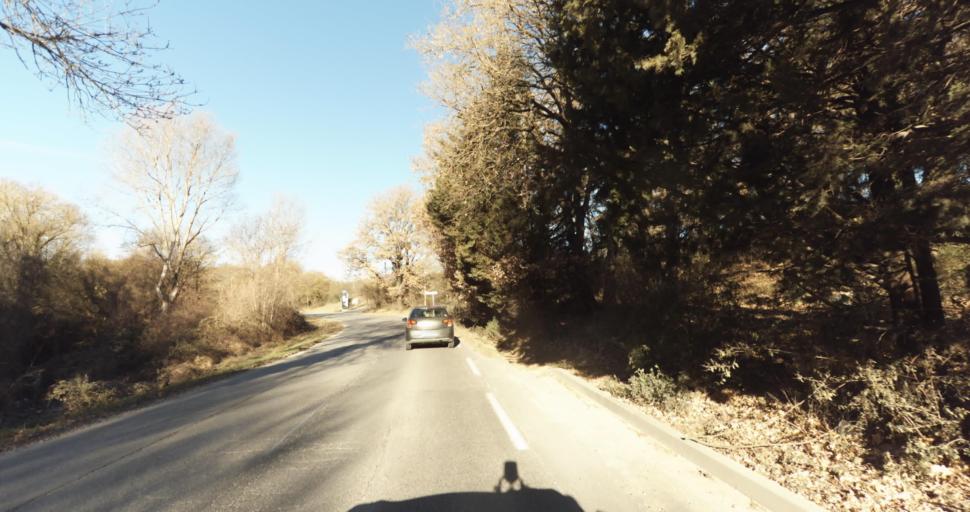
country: FR
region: Provence-Alpes-Cote d'Azur
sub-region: Departement des Bouches-du-Rhone
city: Peypin
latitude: 43.3971
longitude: 5.5724
